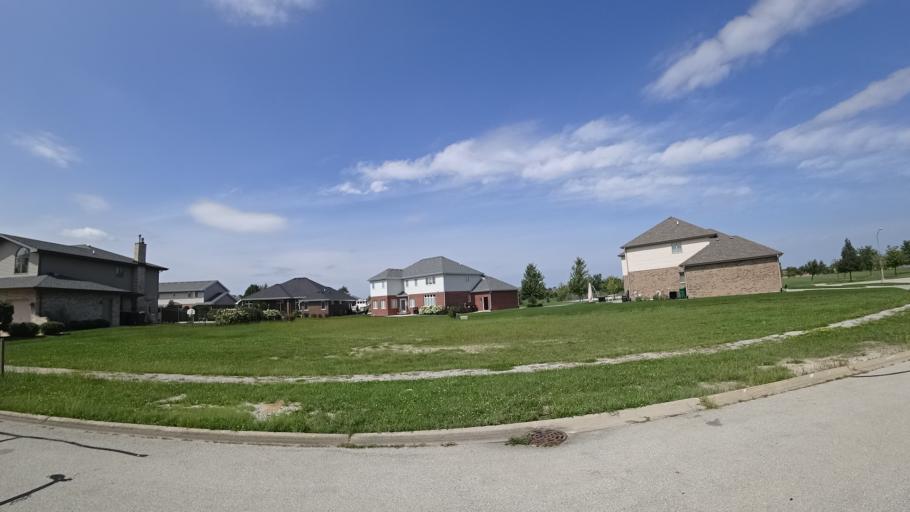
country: US
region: Illinois
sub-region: Cook County
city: Orland Hills
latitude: 41.5698
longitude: -87.8260
